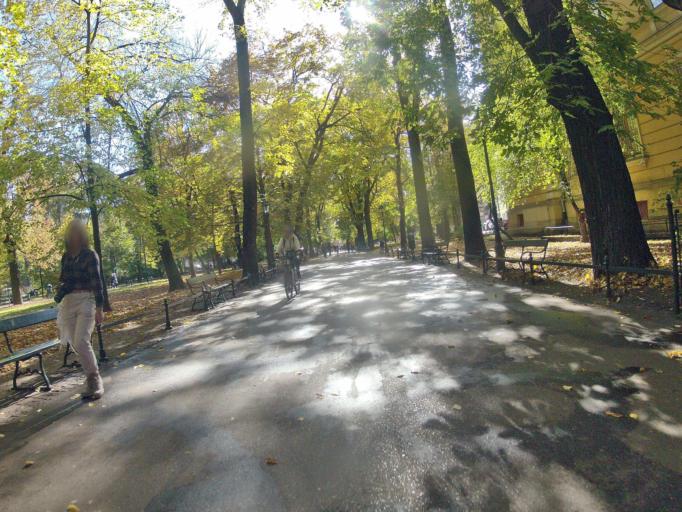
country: PL
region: Lesser Poland Voivodeship
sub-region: Krakow
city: Krakow
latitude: 50.0629
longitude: 19.9441
